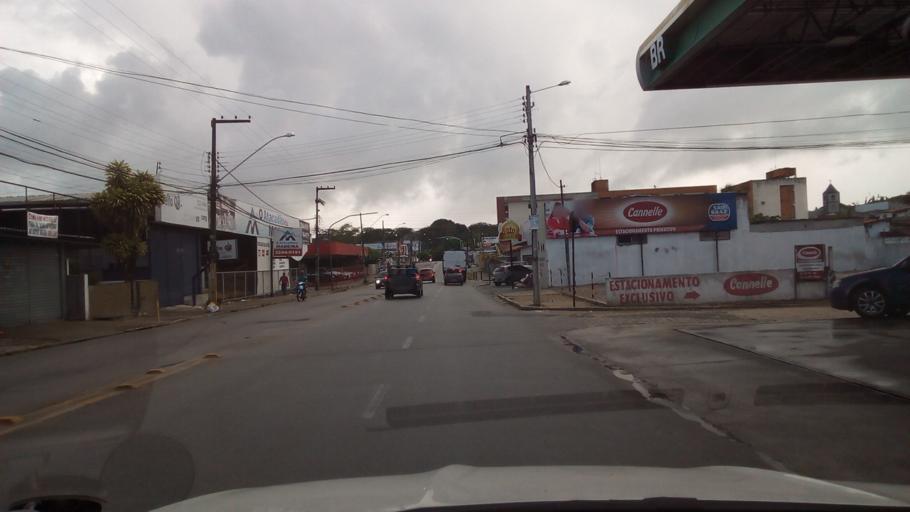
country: BR
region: Paraiba
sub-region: Joao Pessoa
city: Joao Pessoa
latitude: -7.1280
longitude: -34.8613
